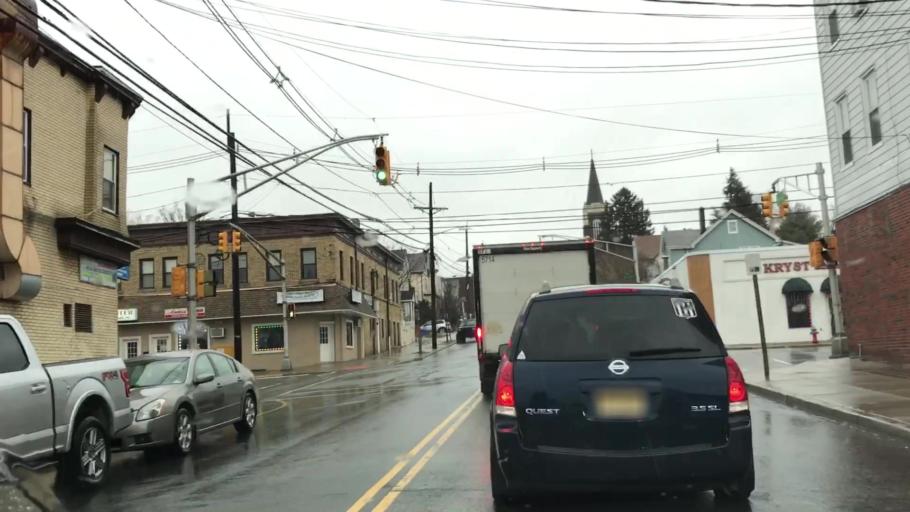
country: US
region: New Jersey
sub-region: Bergen County
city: Garfield
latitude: 40.8748
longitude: -74.1103
